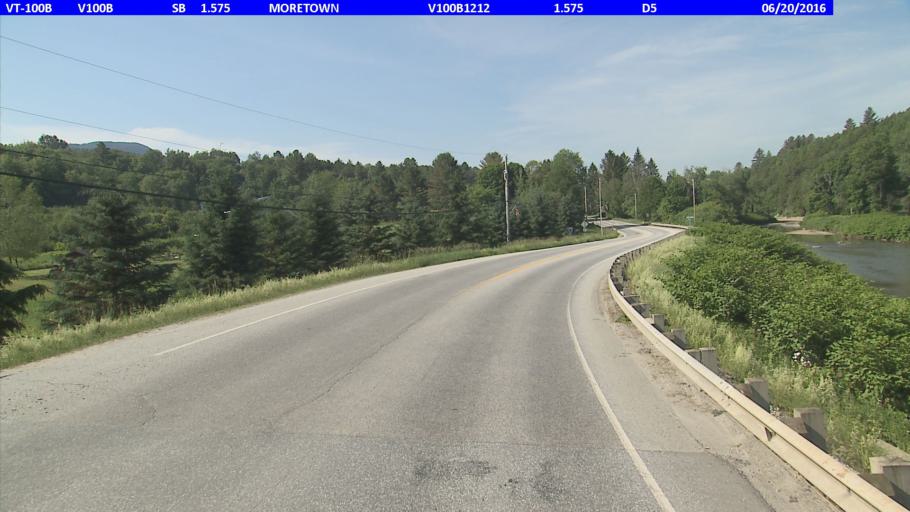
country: US
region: Vermont
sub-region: Washington County
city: Waterbury
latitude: 44.2558
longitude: -72.7572
